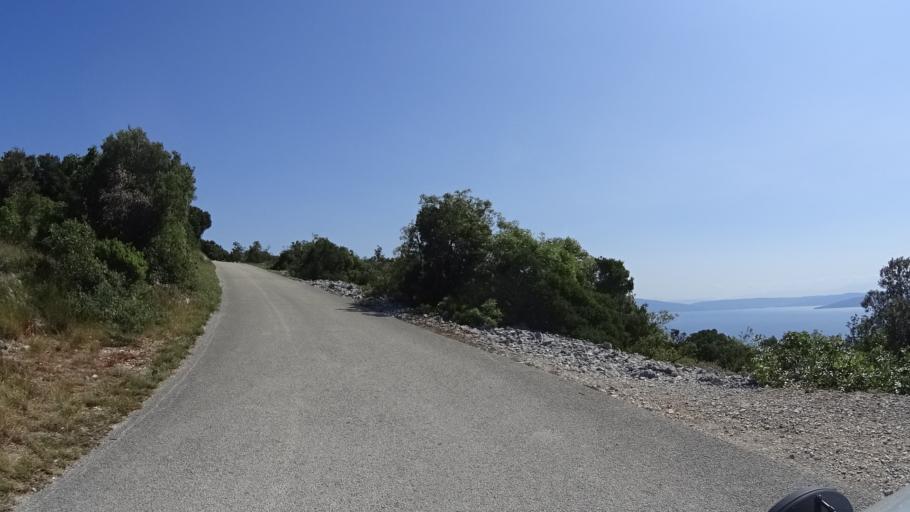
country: HR
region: Istarska
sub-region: Grad Labin
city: Rabac
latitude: 44.9691
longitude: 14.1455
